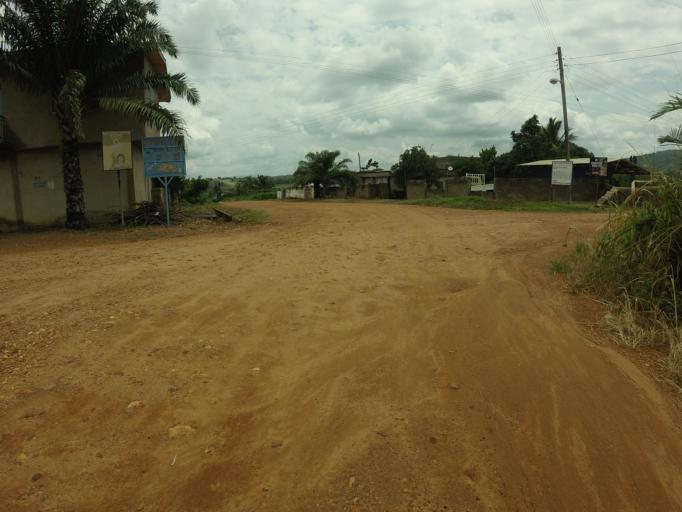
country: GH
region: Volta
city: Ho
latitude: 6.5825
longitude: 0.4587
